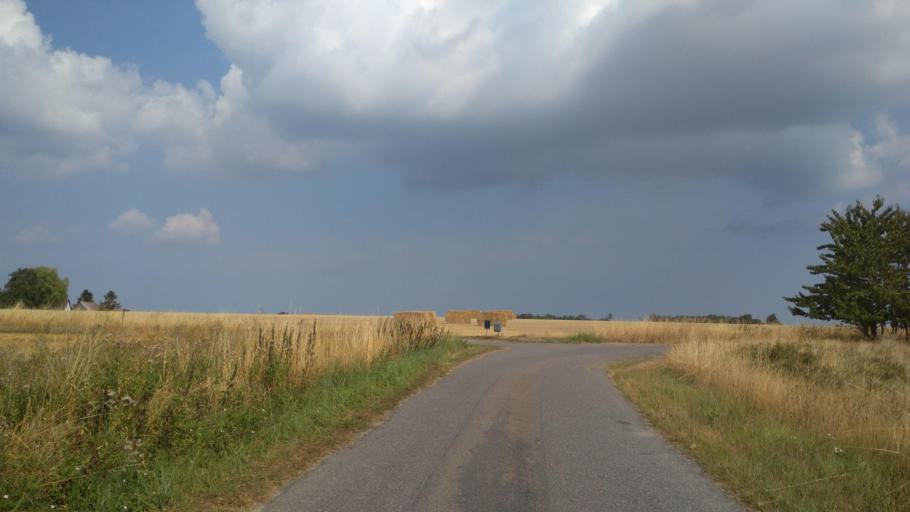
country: DK
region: Capital Region
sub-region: Bornholm Kommune
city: Akirkeby
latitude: 55.0547
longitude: 14.9420
